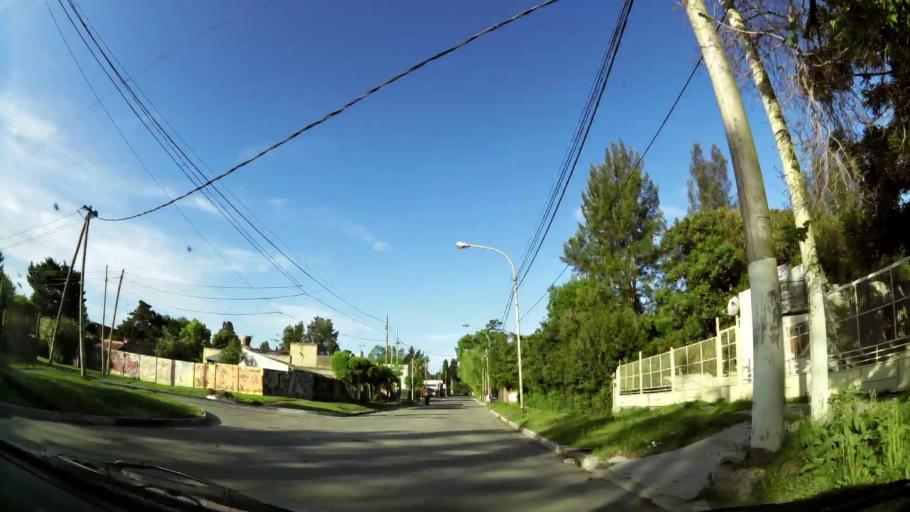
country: AR
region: Buenos Aires
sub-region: Partido de Quilmes
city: Quilmes
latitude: -34.7925
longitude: -58.2093
